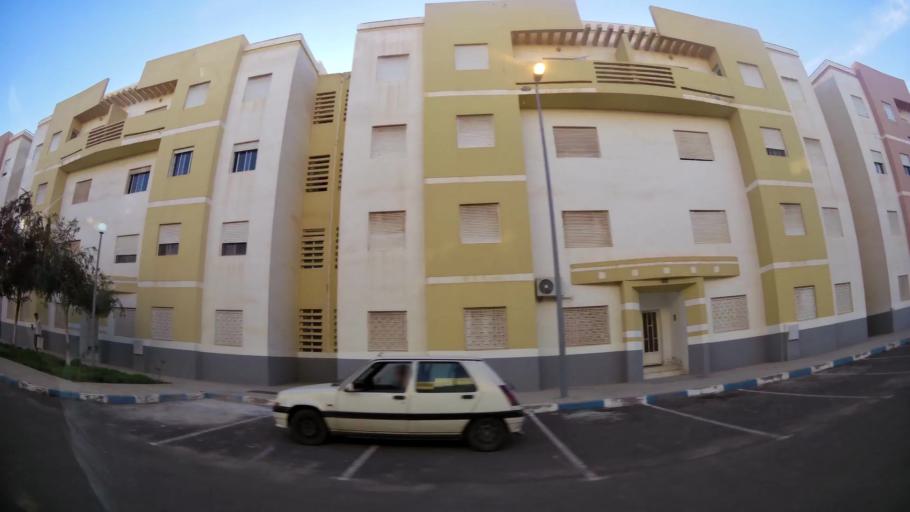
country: MA
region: Oriental
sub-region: Berkane-Taourirt
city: Madagh
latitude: 35.0789
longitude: -2.2368
